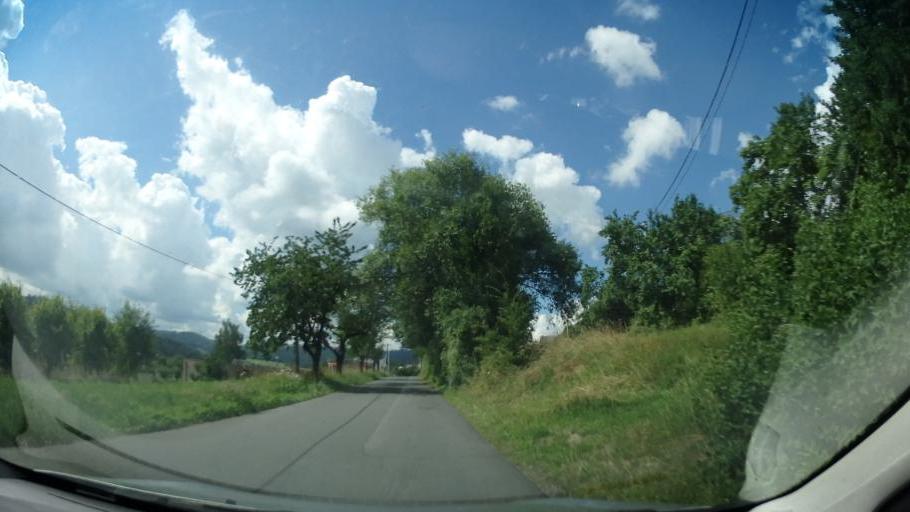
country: CZ
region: Olomoucky
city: Zabreh
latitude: 49.8769
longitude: 16.8493
